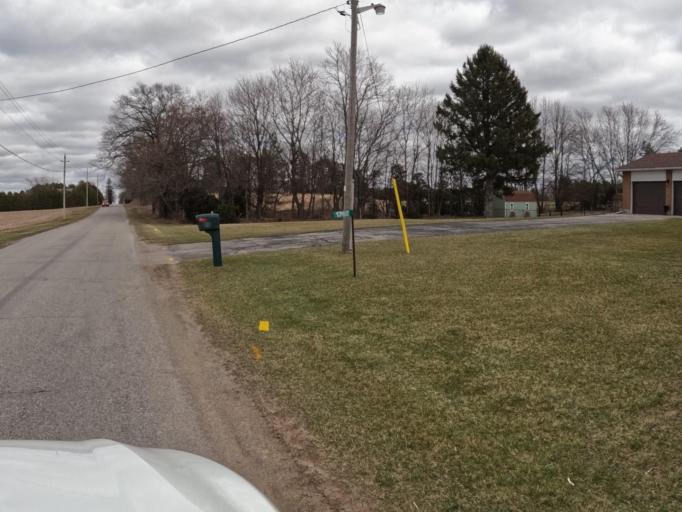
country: CA
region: Ontario
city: Norfolk County
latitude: 42.8126
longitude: -80.3412
